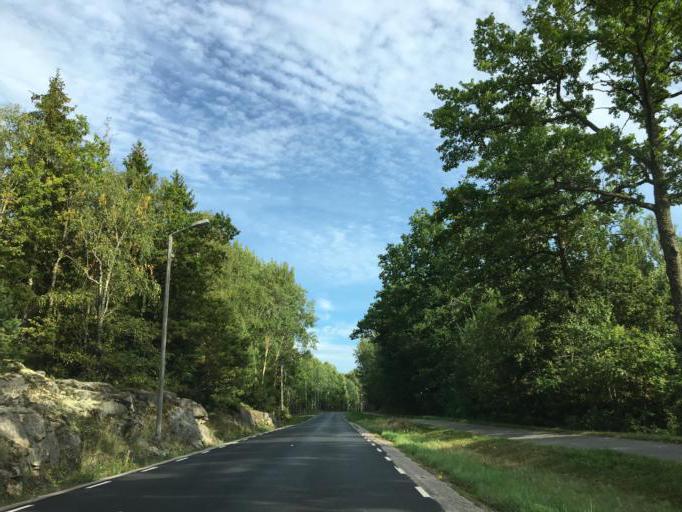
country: SE
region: Soedermanland
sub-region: Eskilstuna Kommun
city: Torshalla
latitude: 59.4491
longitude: 16.4437
